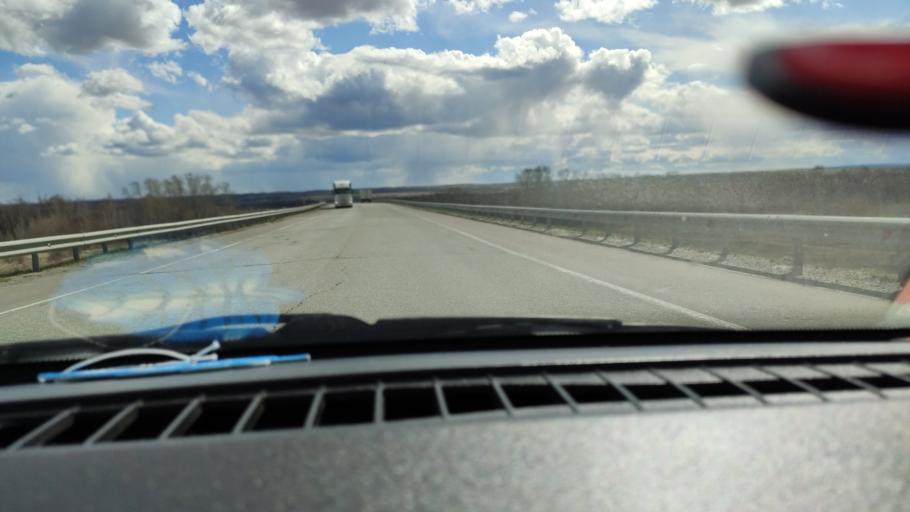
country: RU
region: Samara
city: Varlamovo
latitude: 53.1644
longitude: 48.2820
